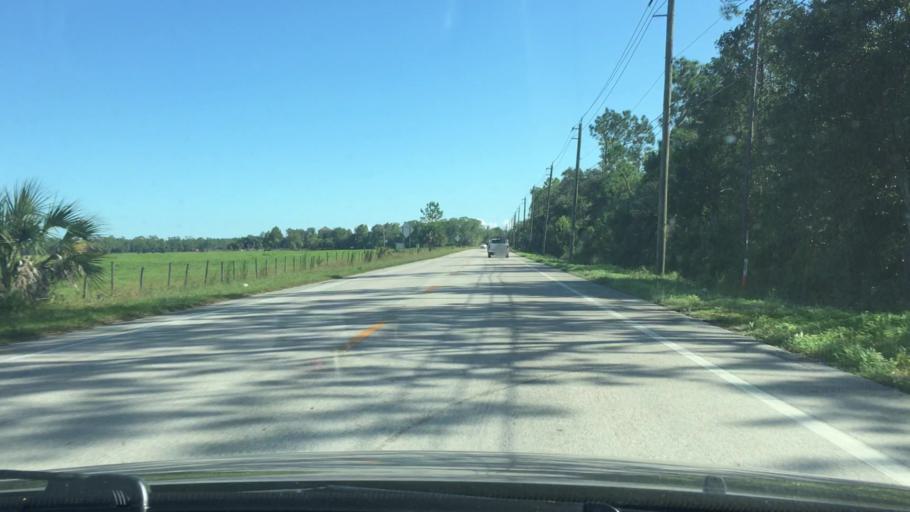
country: US
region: Florida
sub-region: Volusia County
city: South Daytona
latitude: 29.1474
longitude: -81.0809
